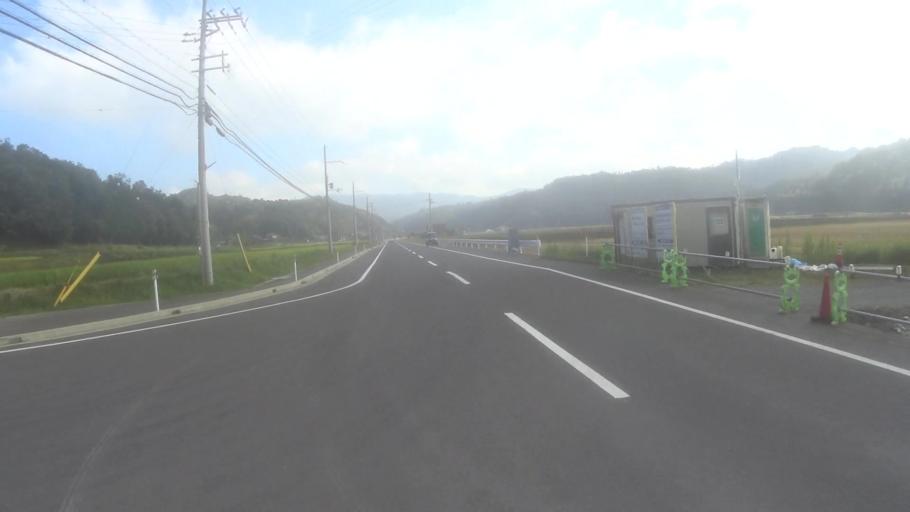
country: JP
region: Kyoto
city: Miyazu
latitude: 35.5776
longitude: 135.1212
